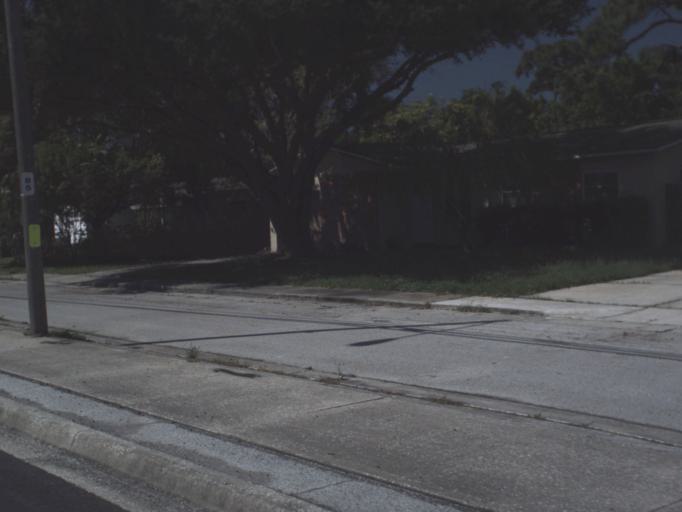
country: US
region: Florida
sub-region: Pinellas County
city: Pinellas Park
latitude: 27.8621
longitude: -82.7290
